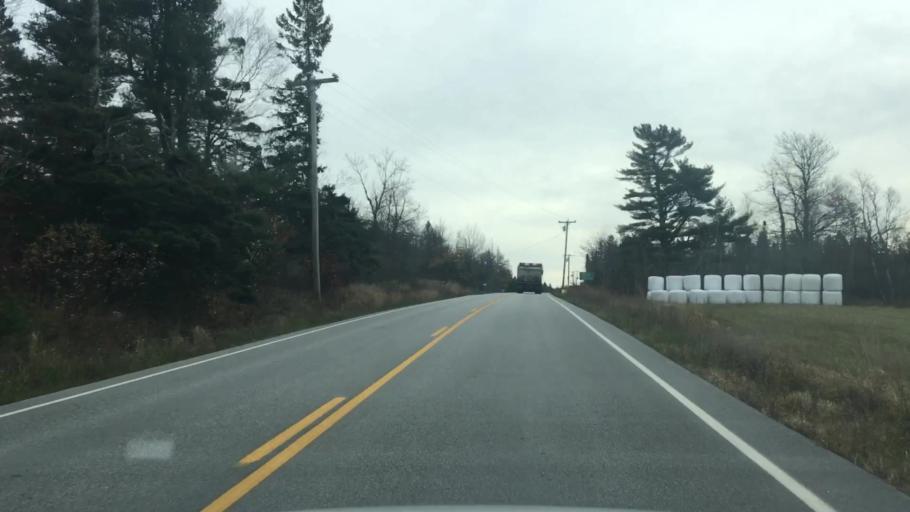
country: US
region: Maine
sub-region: Hancock County
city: Penobscot
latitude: 44.5290
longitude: -68.6708
